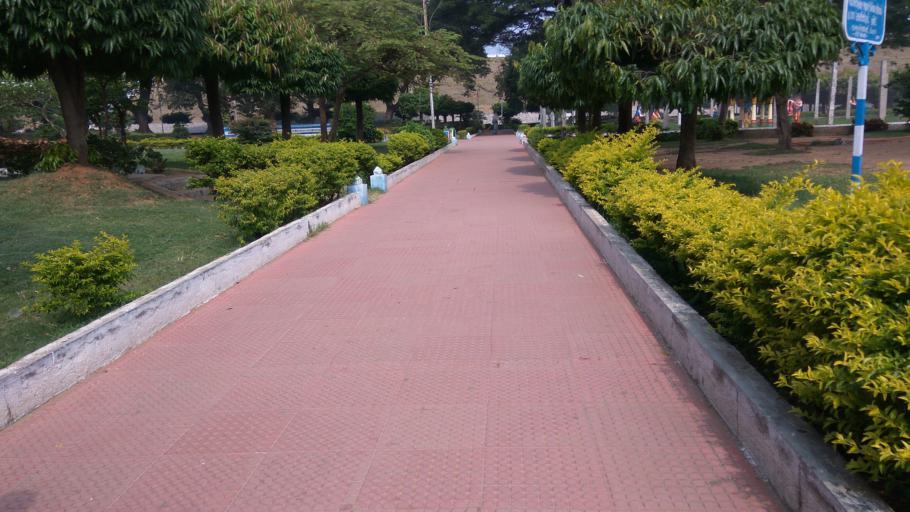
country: IN
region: Tamil Nadu
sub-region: Krishnagiri
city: Krishnagiri
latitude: 12.4738
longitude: 78.1854
